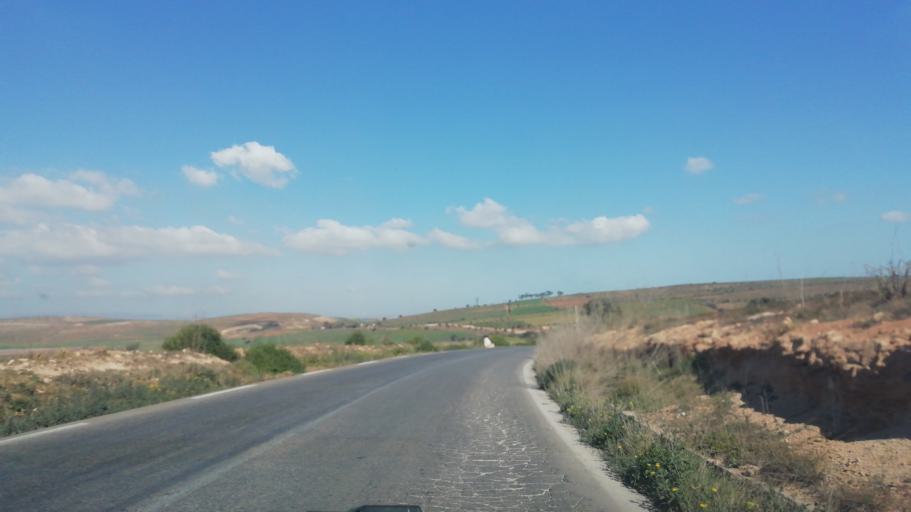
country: DZ
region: Oran
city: Ain el Bya
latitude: 35.7313
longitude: -0.2527
